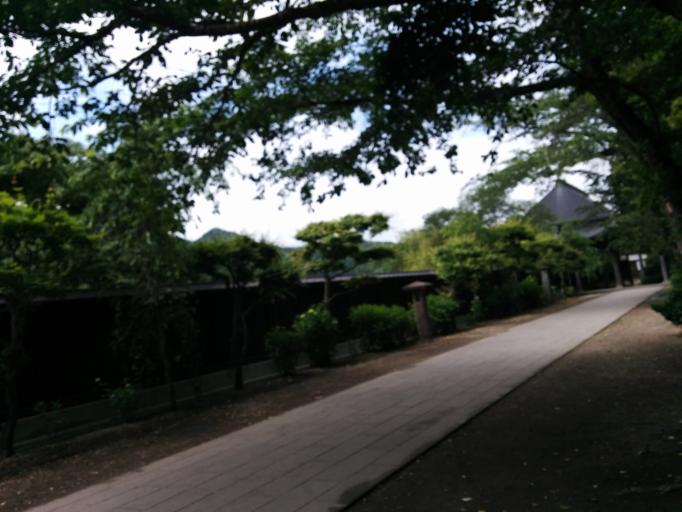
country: JP
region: Yamagata
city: Tendo
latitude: 38.3121
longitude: 140.4357
